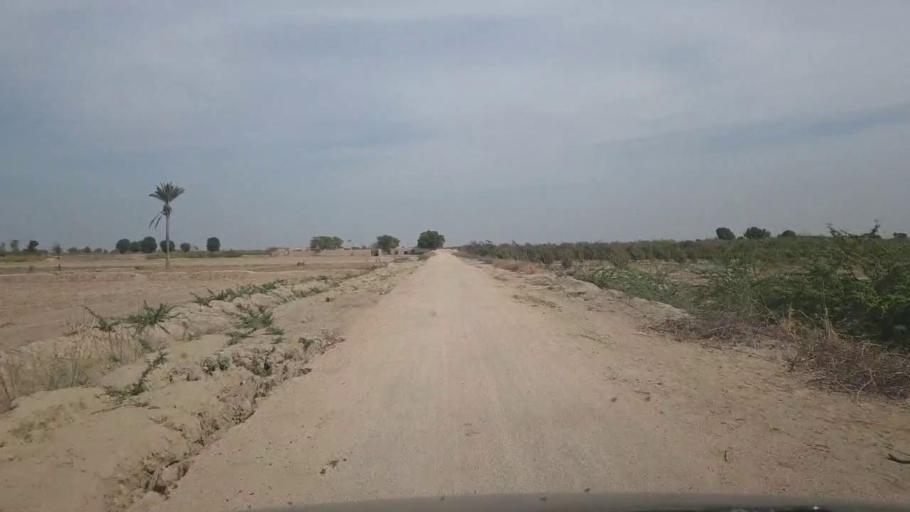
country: PK
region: Sindh
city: Kunri
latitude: 25.2295
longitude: 69.5944
